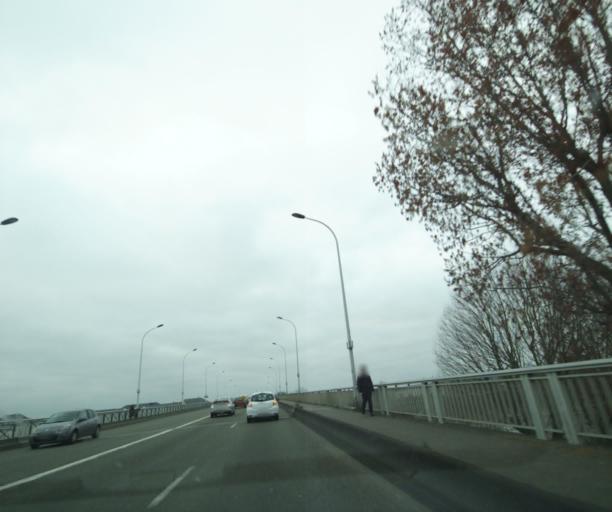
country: FR
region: Ile-de-France
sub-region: Departement des Yvelines
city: Poissy
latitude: 48.9359
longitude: 2.0401
